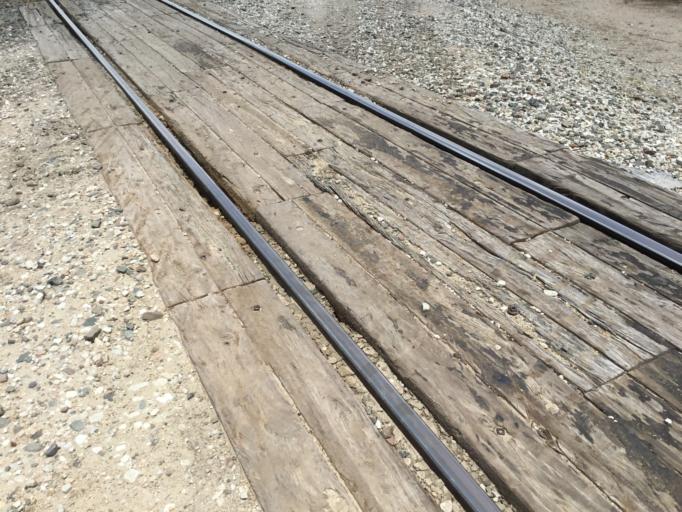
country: US
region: Kansas
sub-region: Republic County
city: Belleville
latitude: 39.7359
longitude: -97.8759
